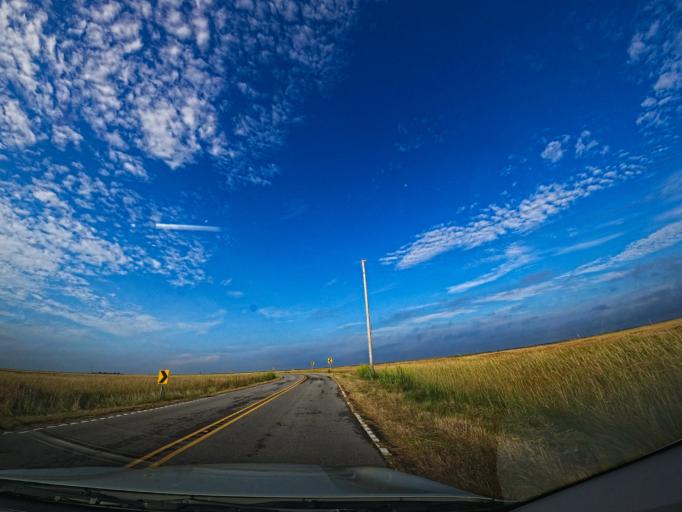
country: US
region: Louisiana
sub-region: Terrebonne Parish
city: Dulac
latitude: 29.3067
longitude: -90.6609
